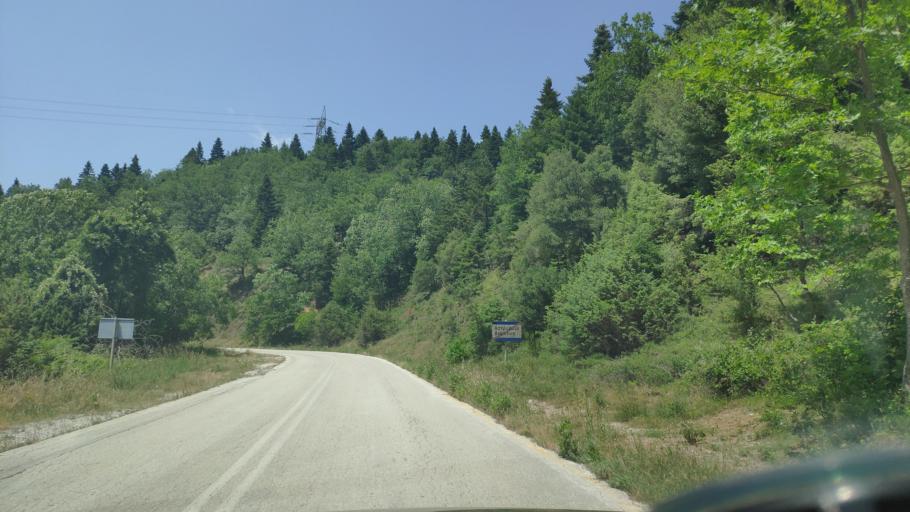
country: GR
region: Epirus
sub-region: Nomos Artas
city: Ano Kalentini
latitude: 39.2739
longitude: 21.2863
